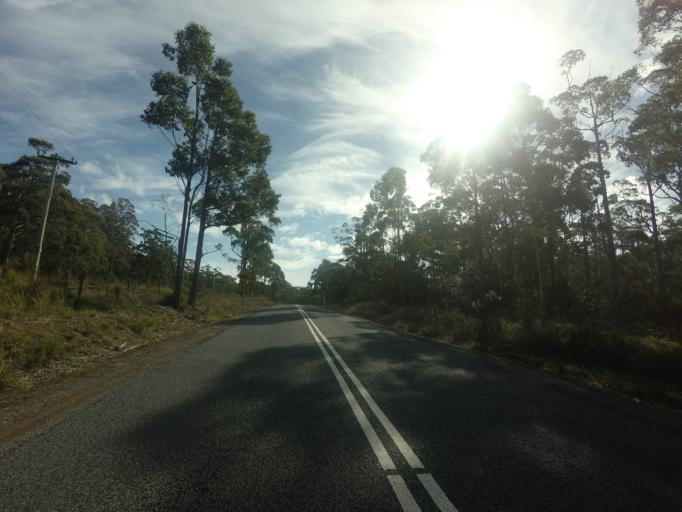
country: AU
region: Tasmania
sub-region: Clarence
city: Sandford
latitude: -43.1242
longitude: 147.7667
